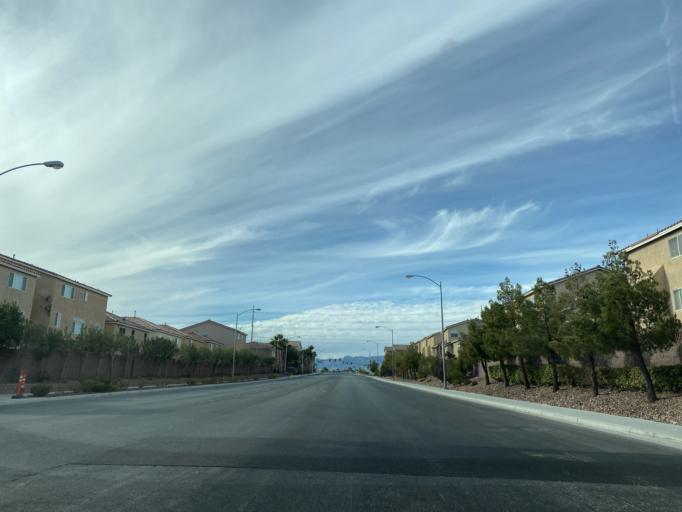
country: US
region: Nevada
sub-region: Clark County
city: Enterprise
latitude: 36.0342
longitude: -115.2400
